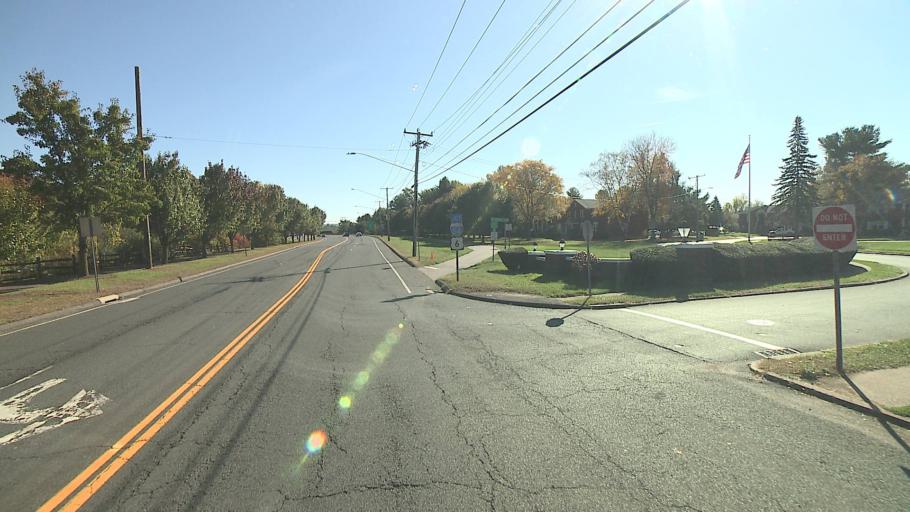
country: US
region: Connecticut
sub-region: Hartford County
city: East Hartford
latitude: 41.7808
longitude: -72.5758
